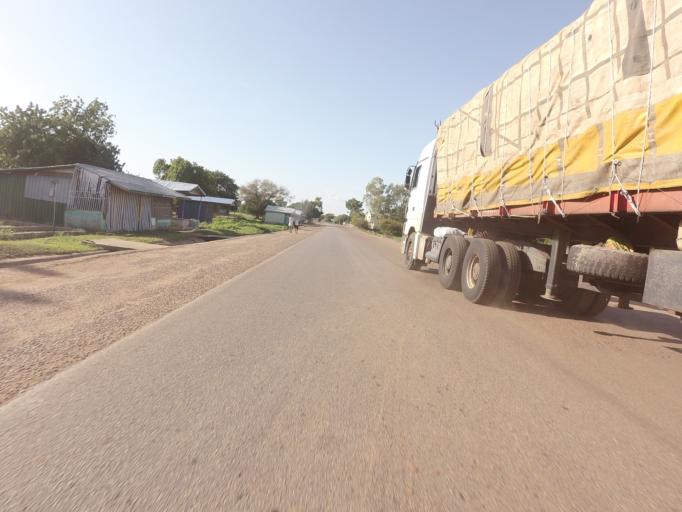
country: GH
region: Upper East
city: Navrongo
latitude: 10.9068
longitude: -1.0908
